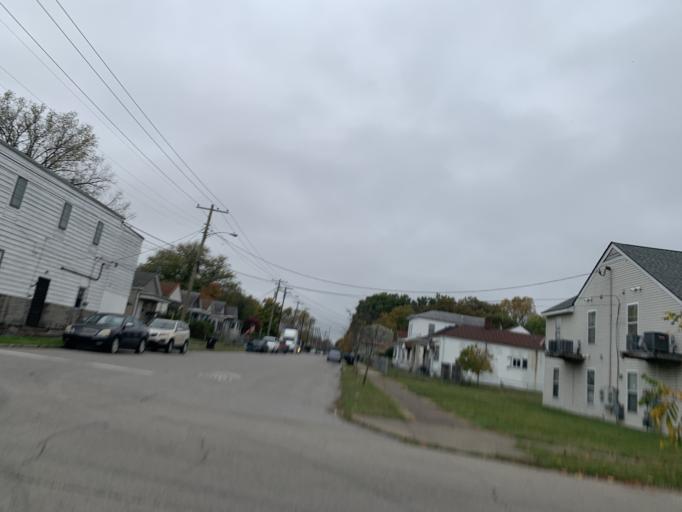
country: US
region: Kentucky
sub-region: Jefferson County
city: Louisville
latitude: 38.2606
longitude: -85.7795
